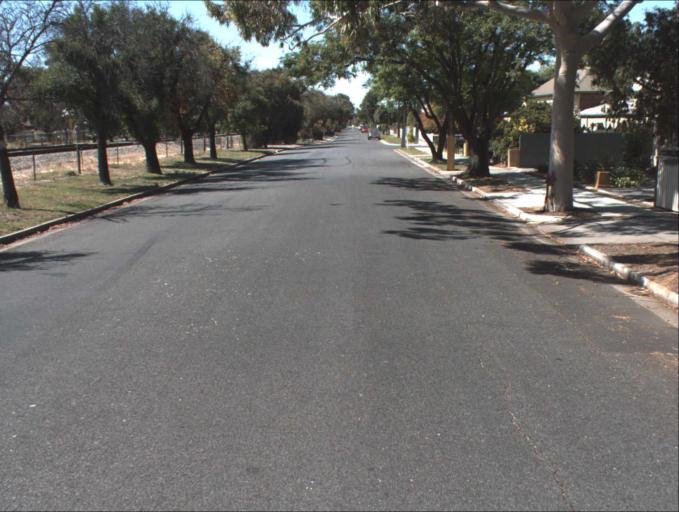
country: AU
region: South Australia
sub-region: Port Adelaide Enfield
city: Alberton
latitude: -34.8614
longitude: 138.5208
